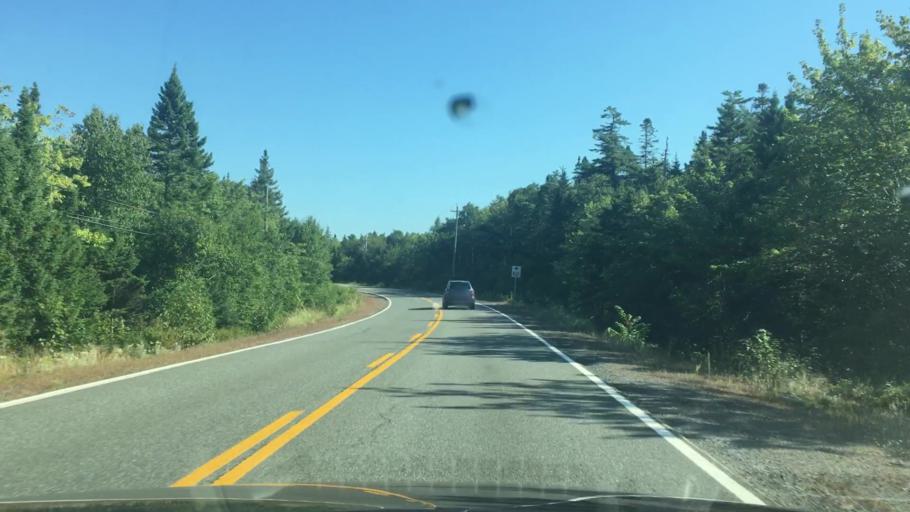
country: CA
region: Nova Scotia
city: Cole Harbour
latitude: 44.8001
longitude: -62.8820
